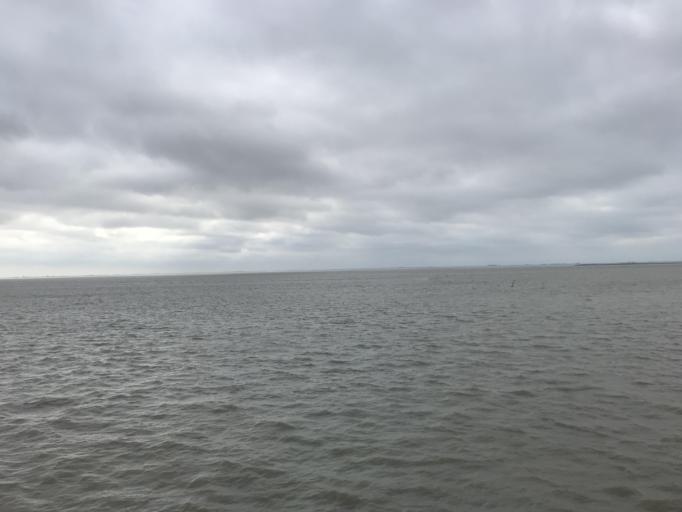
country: DE
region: Lower Saxony
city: Emden
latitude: 53.3289
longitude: 7.0954
